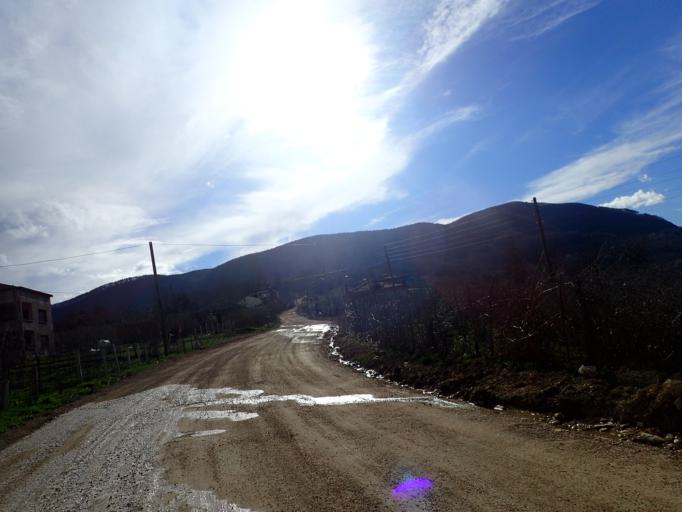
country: TR
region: Ordu
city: Kumru
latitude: 40.9315
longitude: 37.2537
